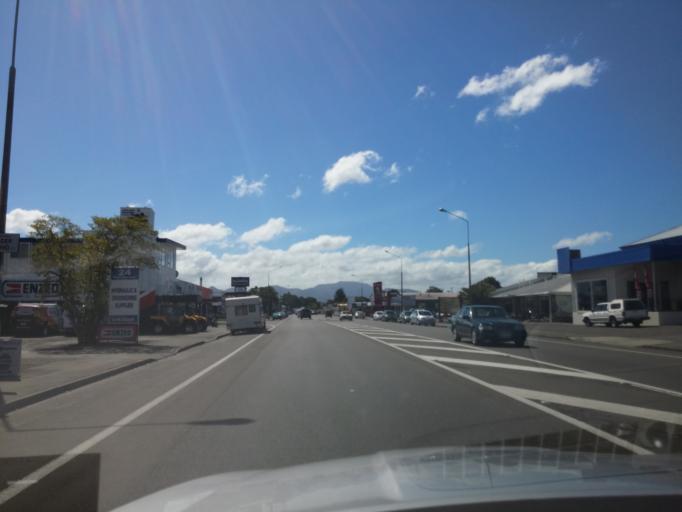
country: NZ
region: Marlborough
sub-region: Marlborough District
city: Blenheim
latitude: -41.5054
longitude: 173.9600
